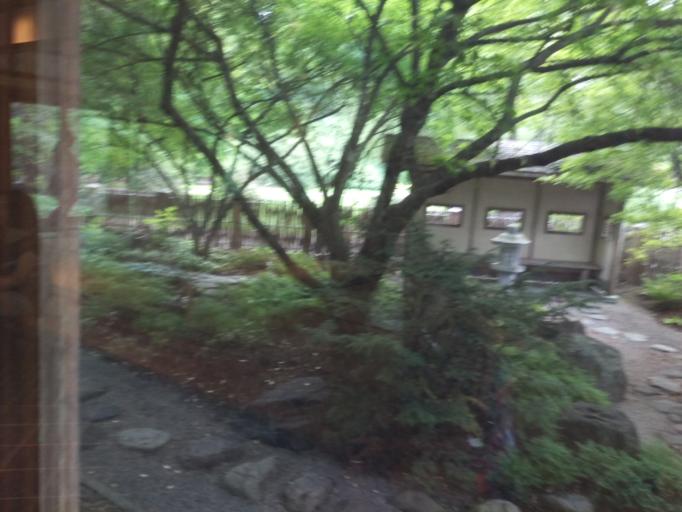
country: CA
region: Quebec
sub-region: Montreal
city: Saint-Leonard
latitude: 45.5604
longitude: -73.5597
